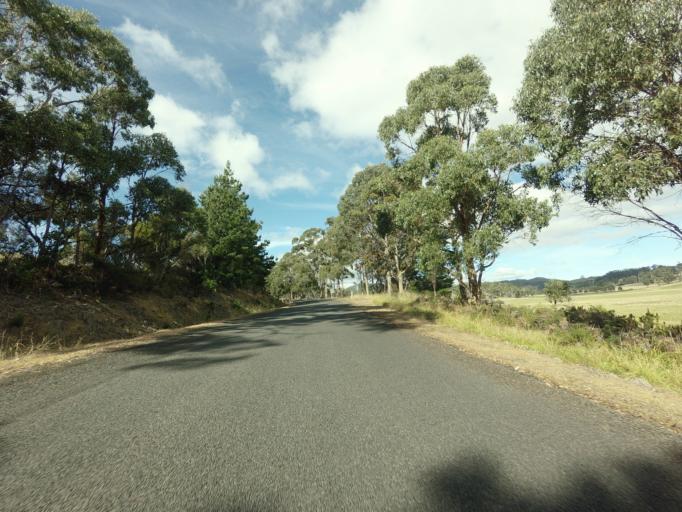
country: AU
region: Tasmania
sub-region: Clarence
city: Sandford
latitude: -43.0455
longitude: 147.7614
